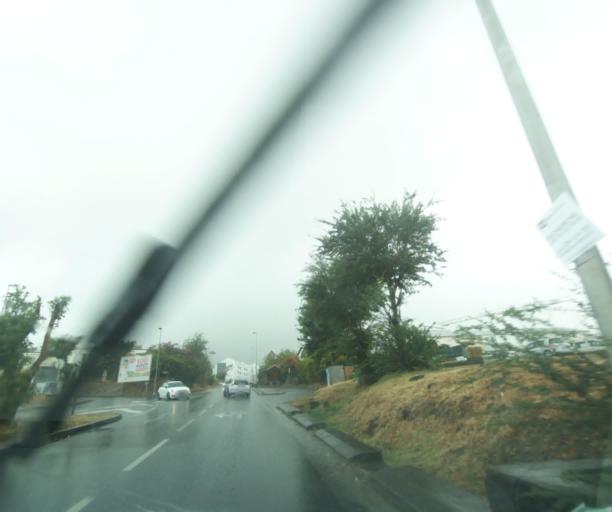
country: RE
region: Reunion
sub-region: Reunion
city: Saint-Paul
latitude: -21.0209
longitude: 55.2657
